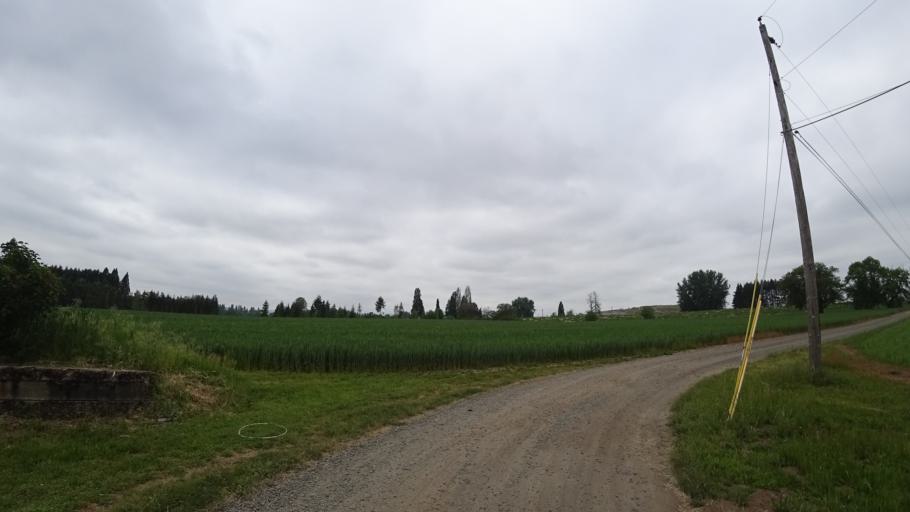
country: US
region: Oregon
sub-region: Washington County
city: Hillsboro
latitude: 45.4865
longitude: -122.9704
